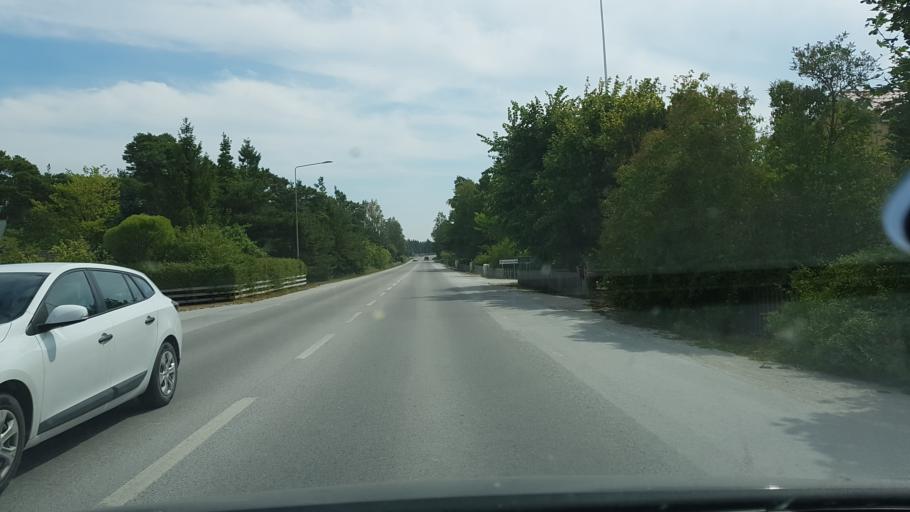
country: SE
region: Gotland
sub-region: Gotland
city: Slite
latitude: 57.7193
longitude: 18.7912
